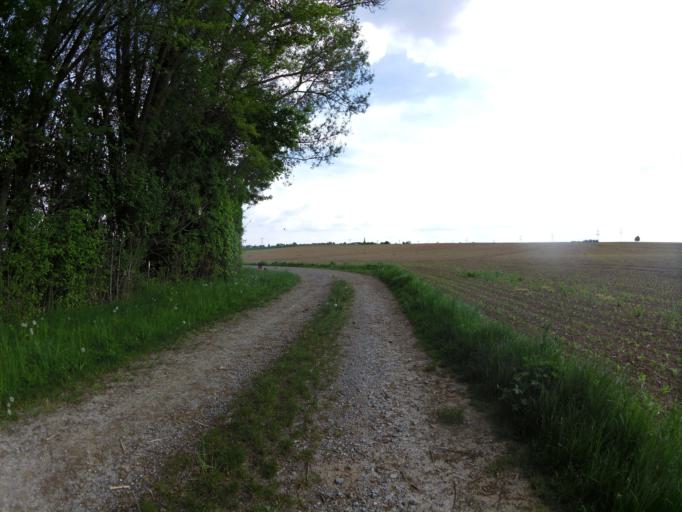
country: DE
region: Bavaria
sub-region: Regierungsbezirk Unterfranken
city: Giebelstadt
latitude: 49.6168
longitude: 9.9410
